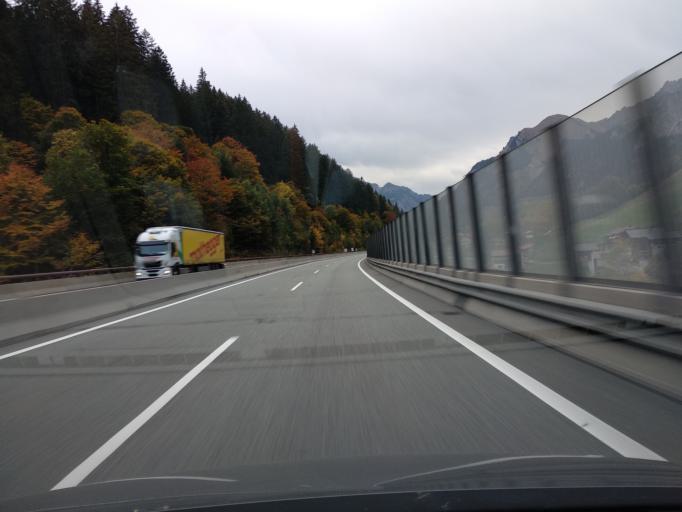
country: AT
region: Vorarlberg
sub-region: Politischer Bezirk Bludenz
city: Klosterle
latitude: 47.1297
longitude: 10.0975
